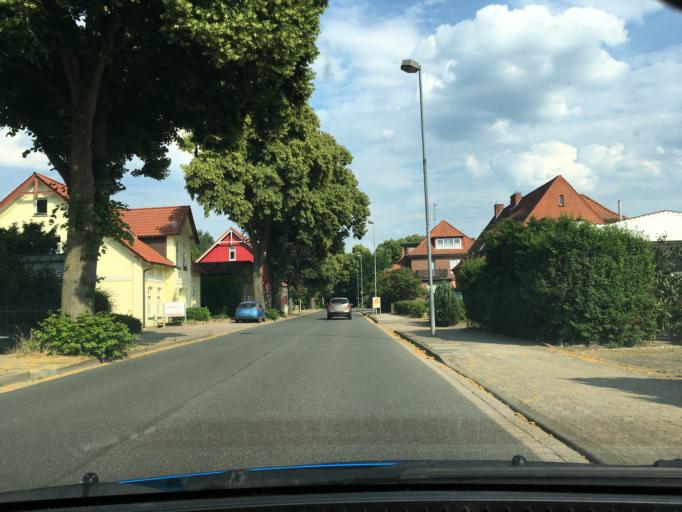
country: DE
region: Lower Saxony
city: Bad Bevensen
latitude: 53.0808
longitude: 10.5694
